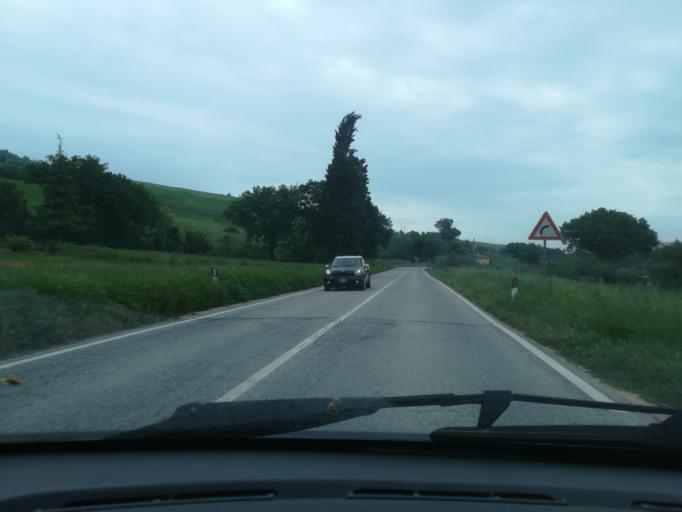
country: IT
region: The Marches
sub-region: Provincia di Macerata
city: Tolentino
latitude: 43.2632
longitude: 13.2433
